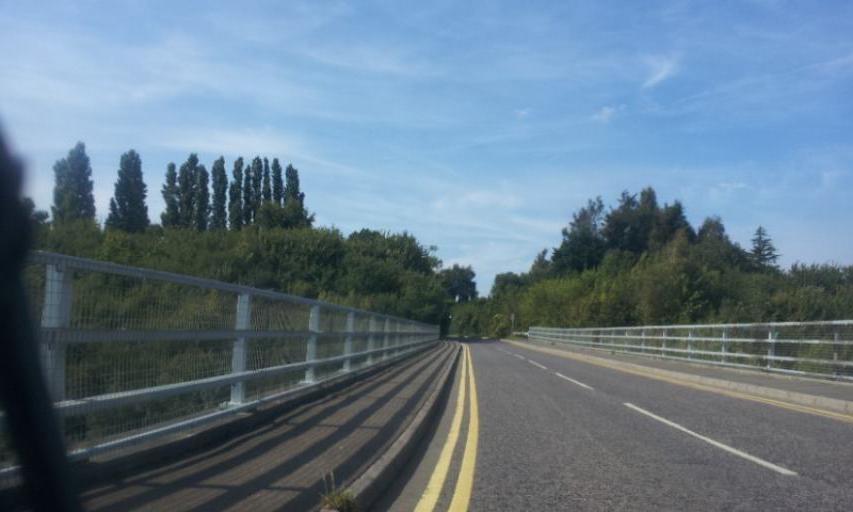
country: GB
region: England
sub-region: Kent
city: Newington
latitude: 51.3360
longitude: 0.6709
